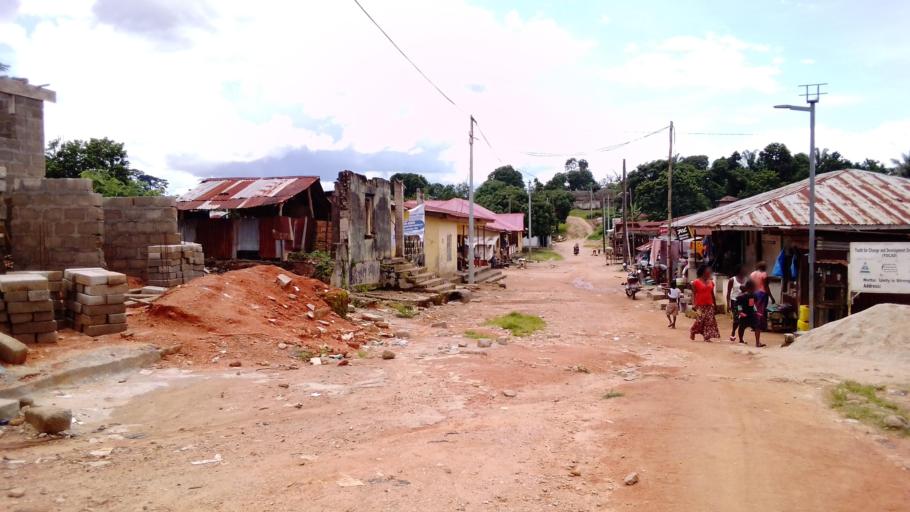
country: SL
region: Eastern Province
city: Koyima
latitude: 8.7015
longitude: -11.0101
